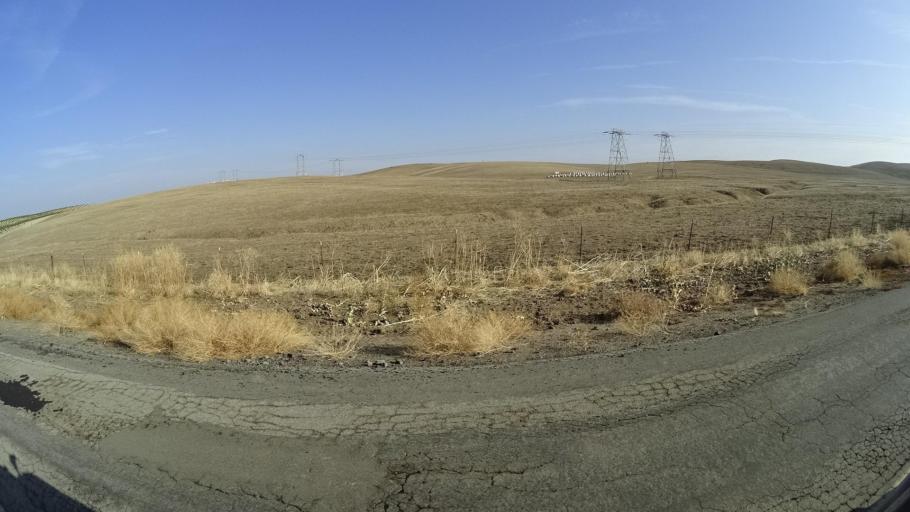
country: US
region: California
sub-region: Tulare County
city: Richgrove
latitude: 35.6407
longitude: -119.0444
